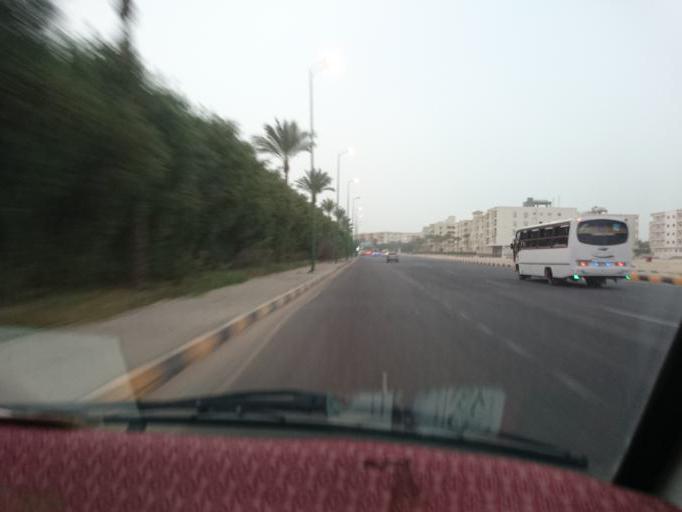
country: EG
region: Red Sea
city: Hurghada
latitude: 27.2010
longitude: 33.8221
